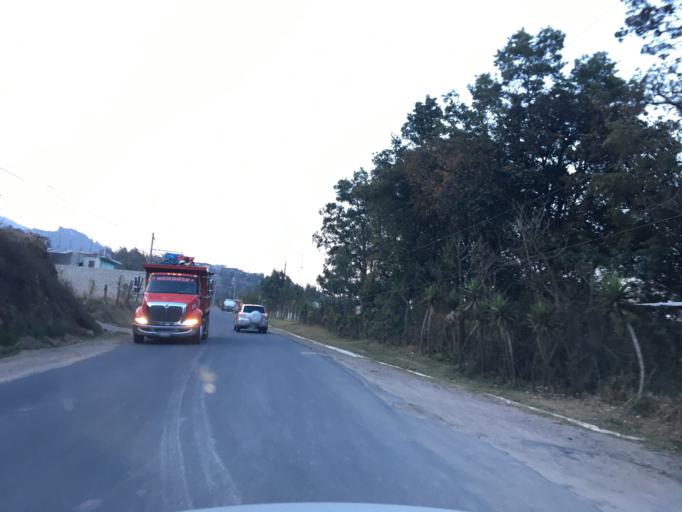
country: GT
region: Chimaltenango
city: Tecpan Guatemala
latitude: 14.7465
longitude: -91.0004
